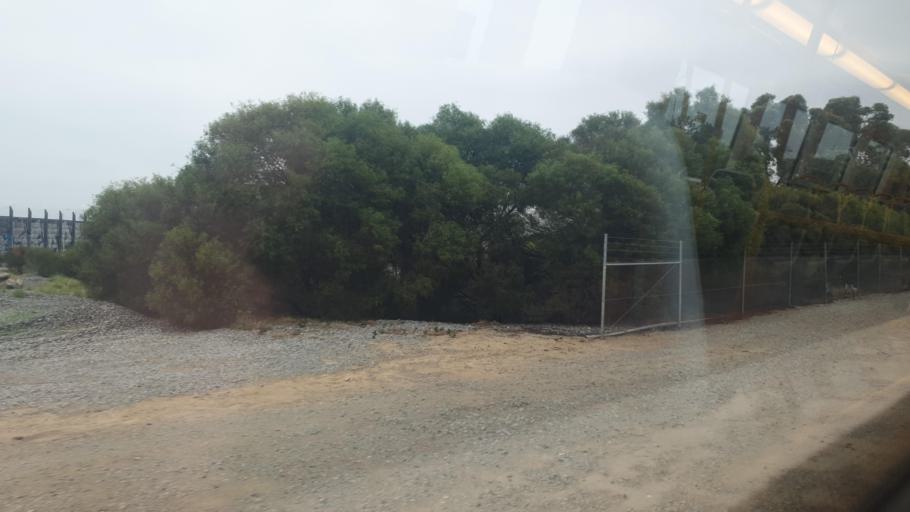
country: AU
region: Western Australia
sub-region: Fremantle
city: North Fremantle
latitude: -32.0366
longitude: 115.7522
